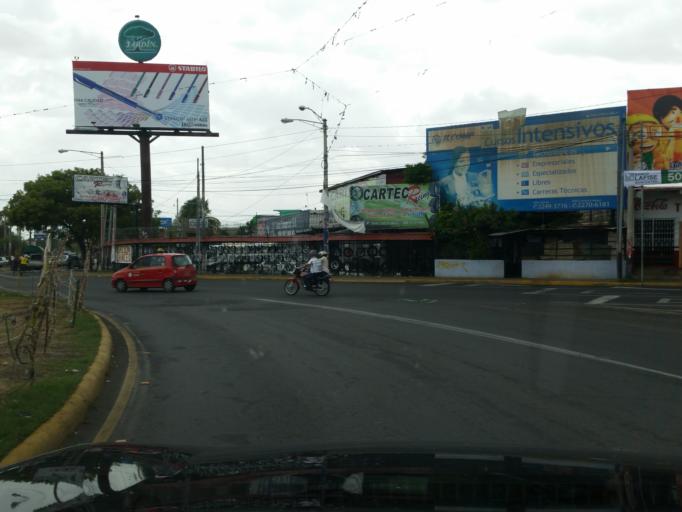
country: NI
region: Managua
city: Managua
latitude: 12.1324
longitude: -86.2575
